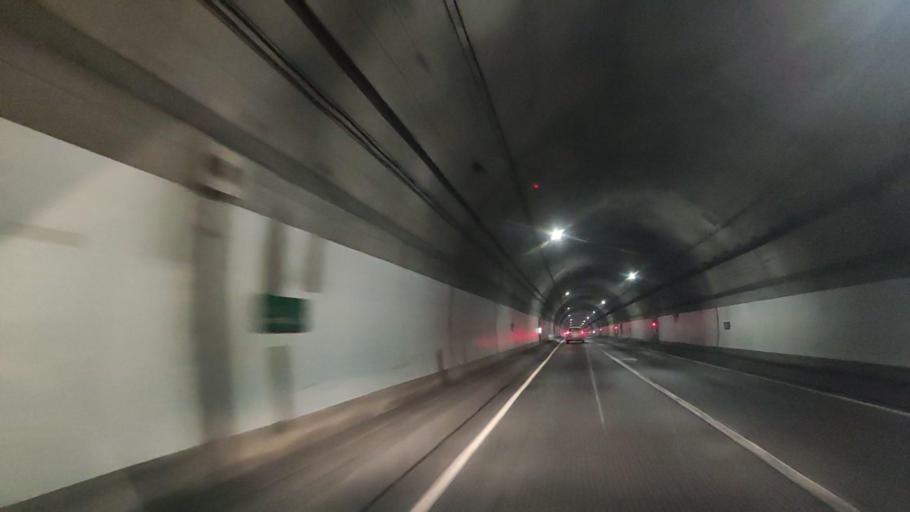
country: JP
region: Hokkaido
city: Rumoi
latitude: 43.7088
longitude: 141.3332
